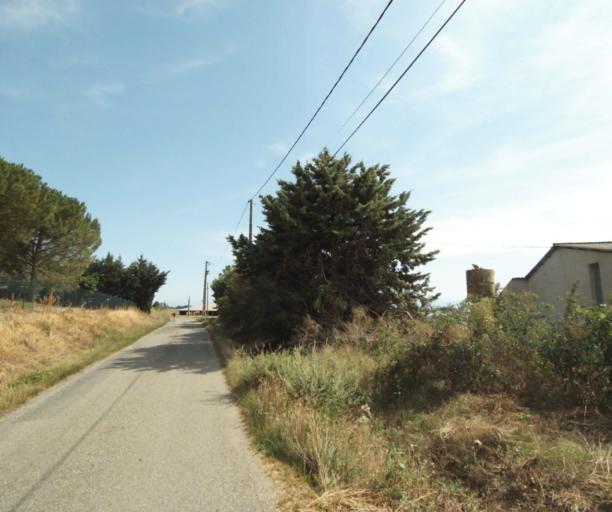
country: FR
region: Midi-Pyrenees
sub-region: Departement de la Haute-Garonne
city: Gaillac-Toulza
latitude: 43.2610
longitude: 1.4170
